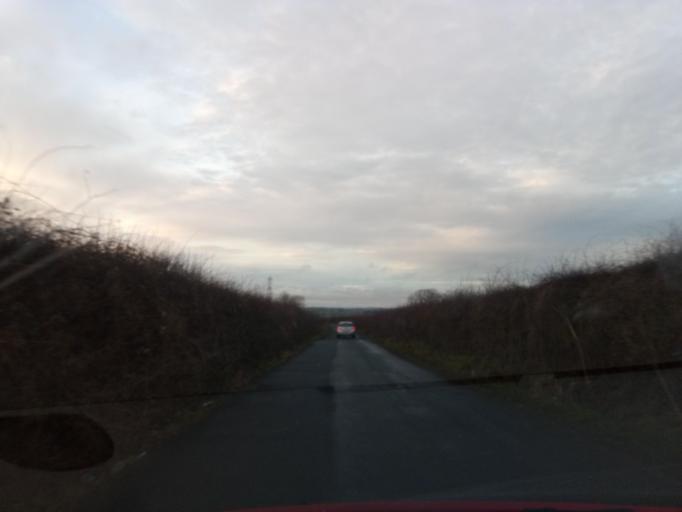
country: GB
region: England
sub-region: Northumberland
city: Ponteland
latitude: 55.0751
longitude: -1.7352
